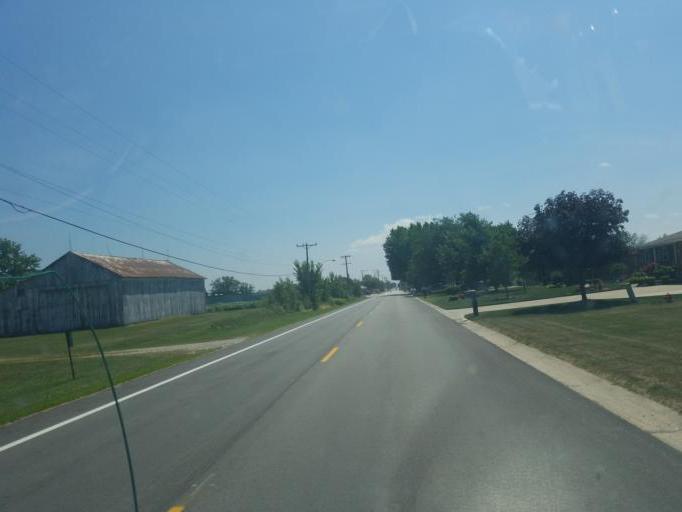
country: US
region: Ohio
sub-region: Shelby County
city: Botkins
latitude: 40.4730
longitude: -84.1828
